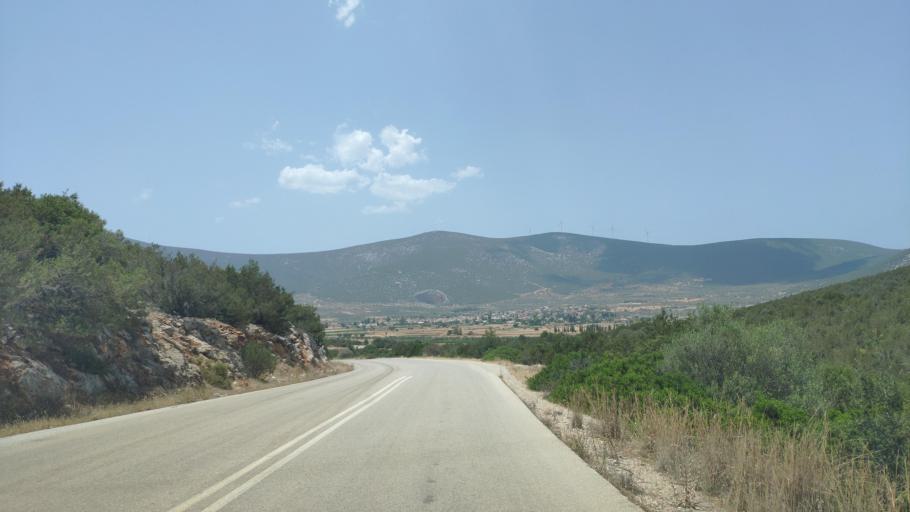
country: GR
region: Peloponnese
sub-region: Nomos Argolidos
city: Didyma
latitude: 37.4452
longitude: 23.1831
